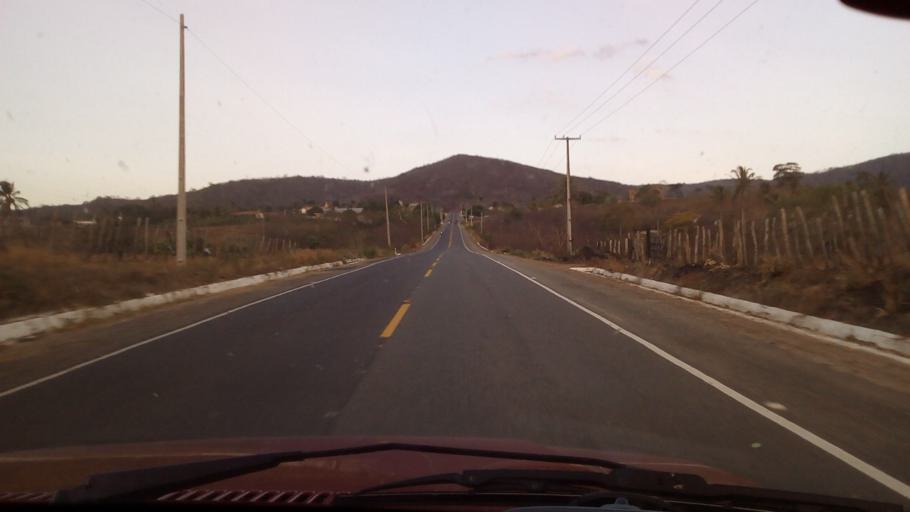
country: BR
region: Paraiba
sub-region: Belem
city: Belem
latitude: -6.7218
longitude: -35.5464
